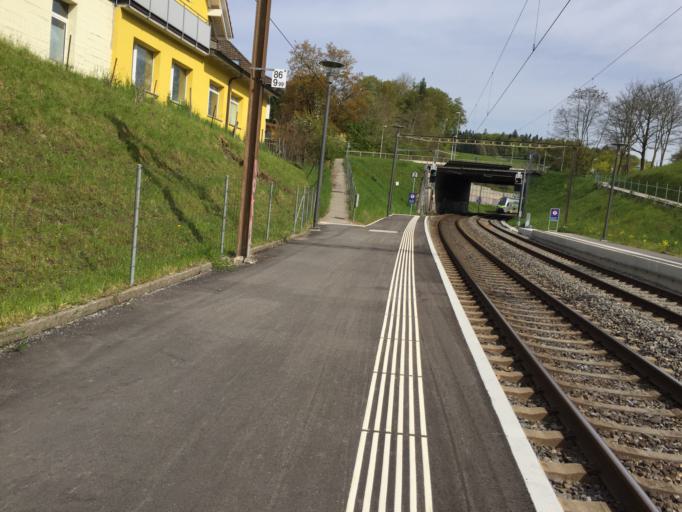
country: CH
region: Fribourg
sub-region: Sense District
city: Flamatt
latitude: 46.8945
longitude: 7.3517
